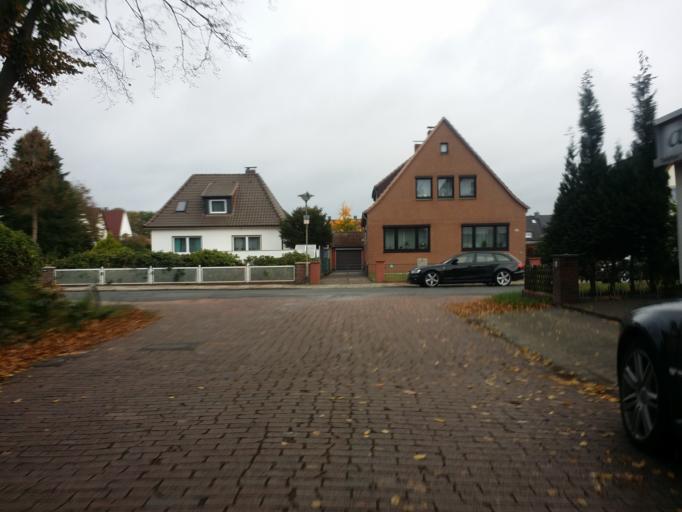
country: DE
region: Lower Saxony
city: Stuhr
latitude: 53.0441
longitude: 8.7389
